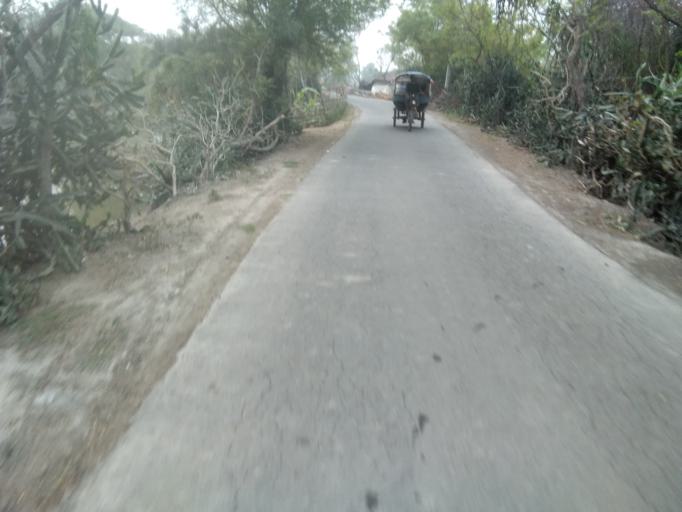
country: BD
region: Khulna
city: Satkhira
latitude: 22.5778
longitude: 89.0727
